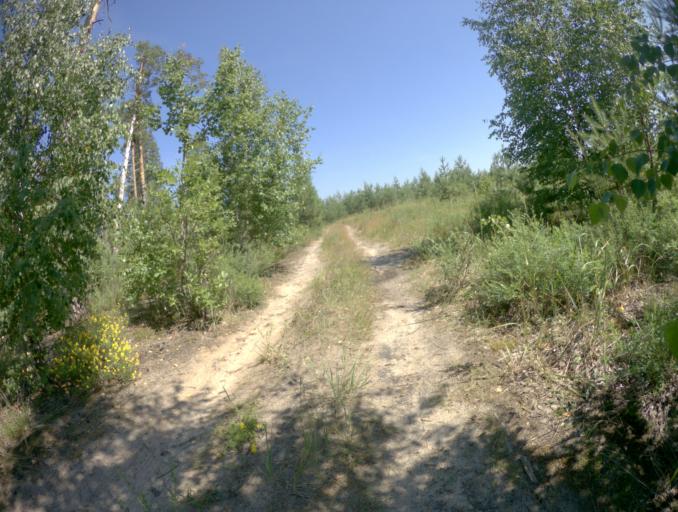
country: RU
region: Ivanovo
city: Talitsy
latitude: 56.4475
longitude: 42.2280
